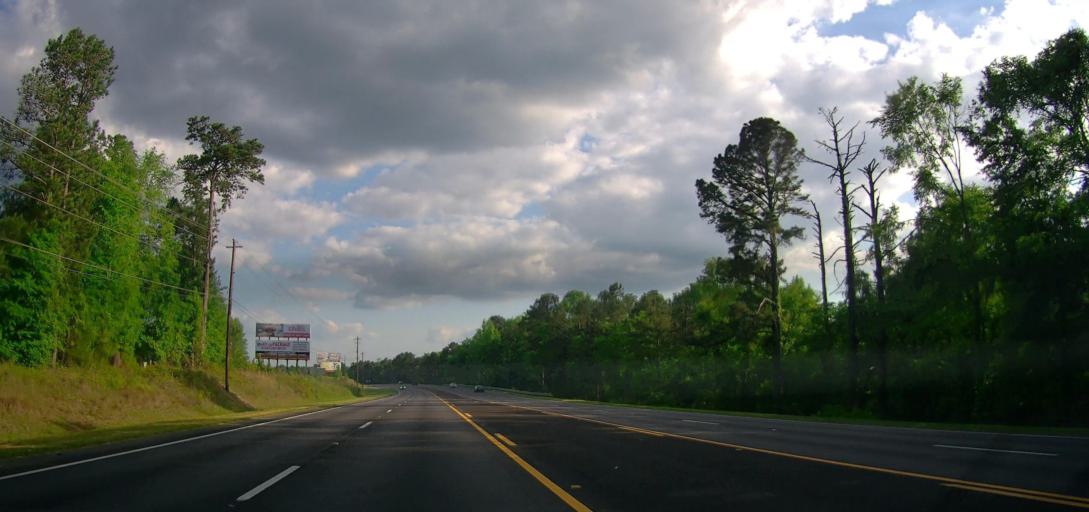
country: US
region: Georgia
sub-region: Baldwin County
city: Milledgeville
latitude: 33.1380
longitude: -83.2708
